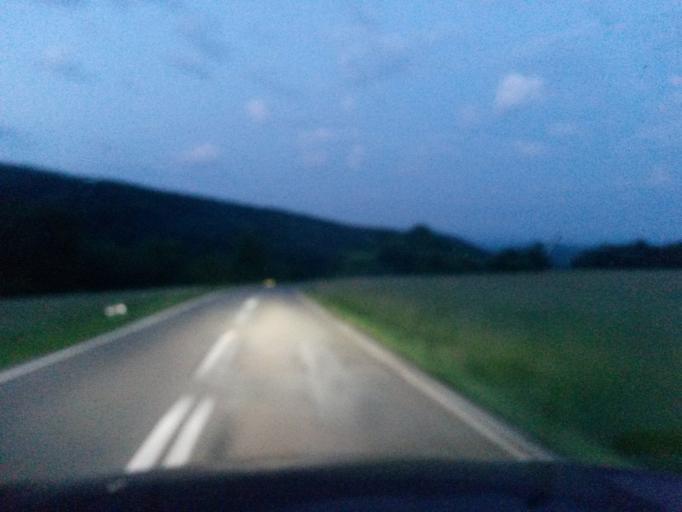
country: SK
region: Presovsky
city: Snina
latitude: 48.9335
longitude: 22.2852
